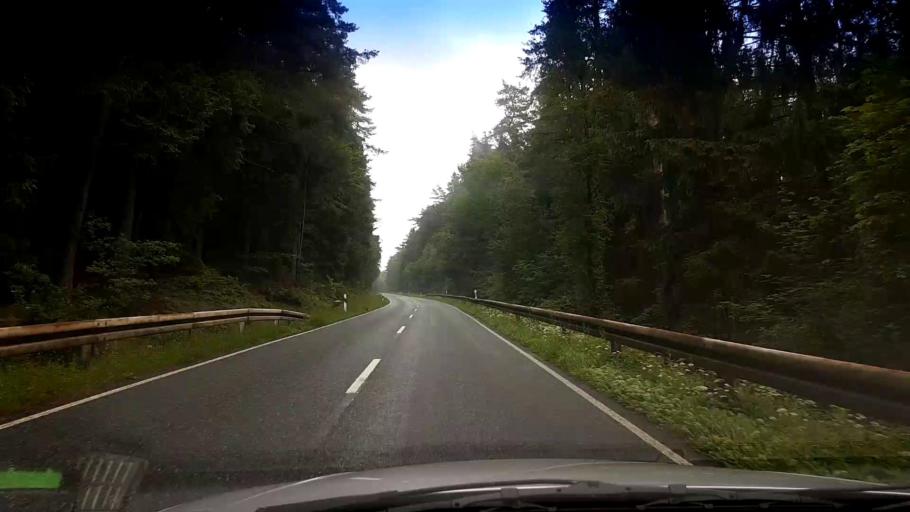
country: DE
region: Bavaria
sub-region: Upper Franconia
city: Weismain
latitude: 50.0870
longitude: 11.2577
